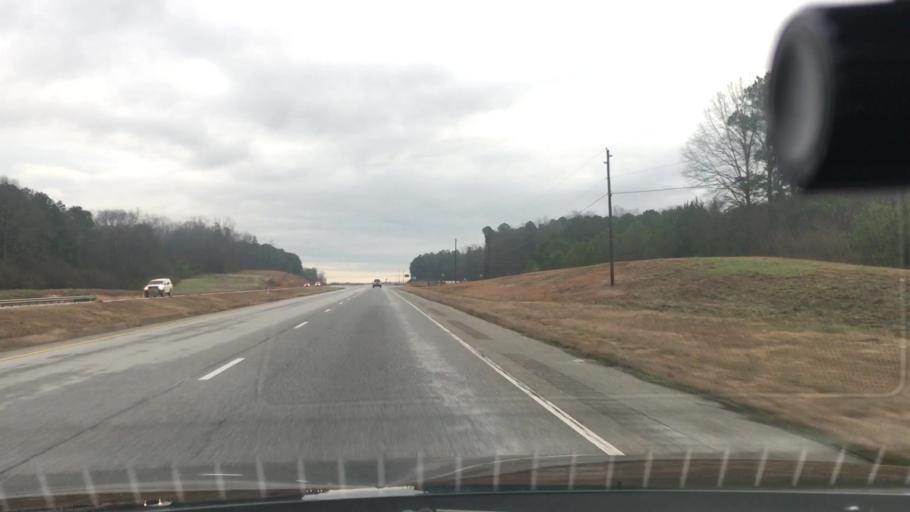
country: US
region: Georgia
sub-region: Spalding County
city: East Griffin
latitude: 33.2521
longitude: -84.1449
